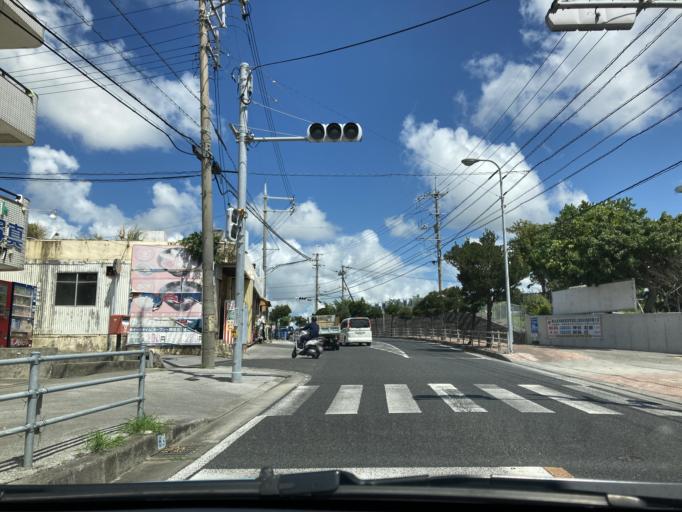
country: JP
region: Okinawa
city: Tomigusuku
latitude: 26.1710
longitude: 127.7220
